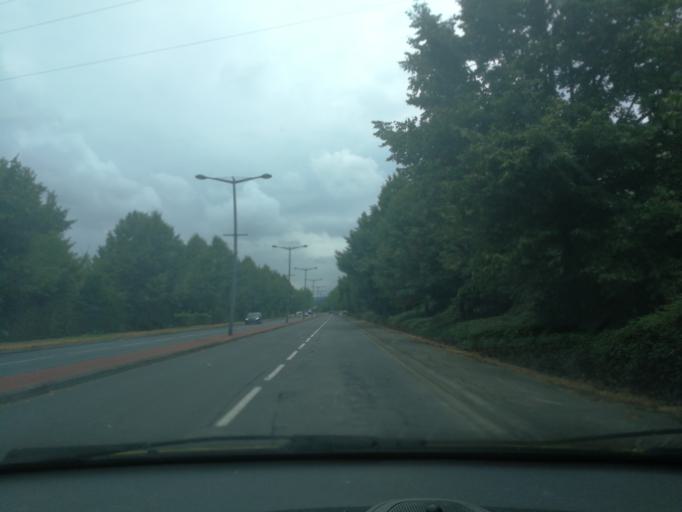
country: FR
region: Lorraine
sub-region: Departement de la Moselle
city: Terville
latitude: 49.3569
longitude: 6.1310
